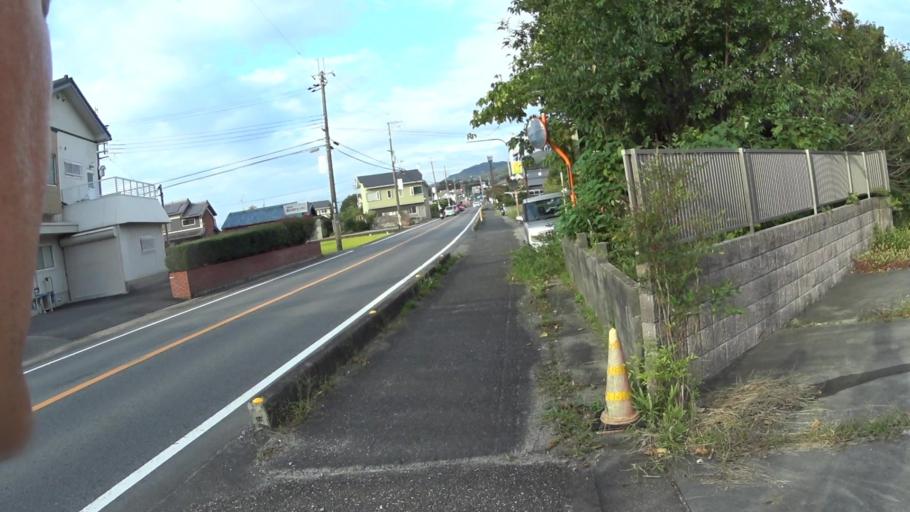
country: JP
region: Nara
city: Tenri
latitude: 34.5455
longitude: 135.8438
